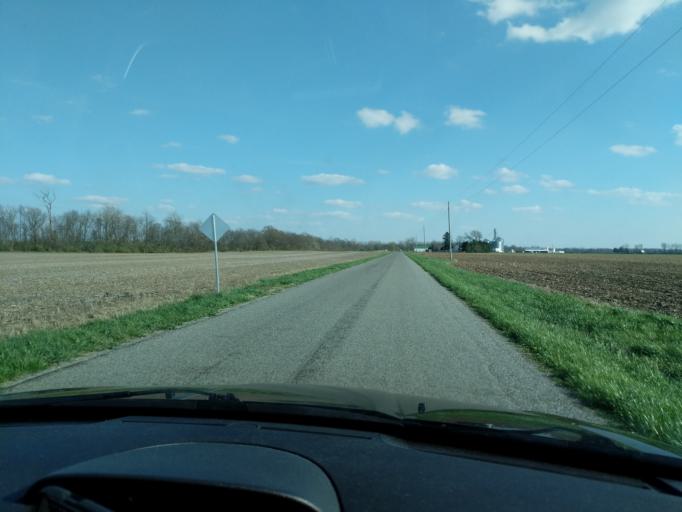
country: US
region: Ohio
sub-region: Champaign County
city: Urbana
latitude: 40.1142
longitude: -83.8049
